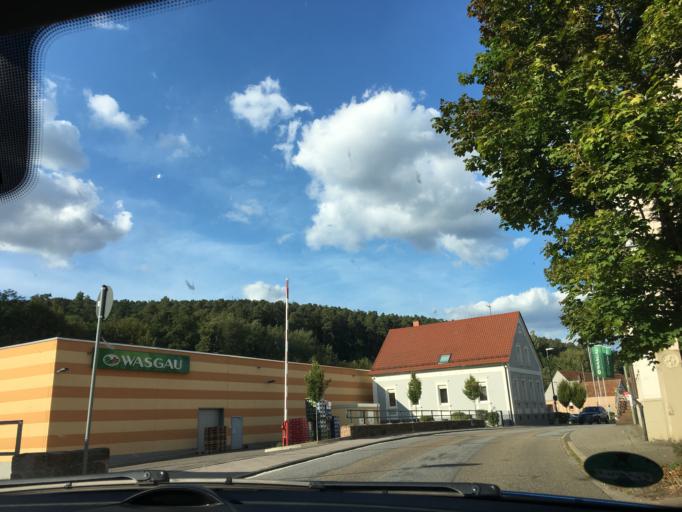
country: DE
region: Rheinland-Pfalz
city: Waldfischbach-Burgalben
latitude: 49.2859
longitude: 7.6486
